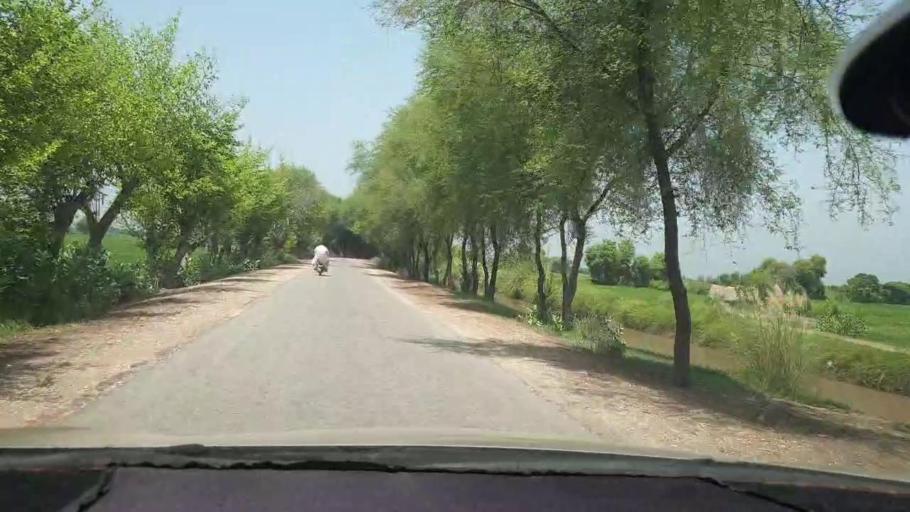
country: PK
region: Sindh
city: Kambar
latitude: 27.6405
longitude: 67.9748
